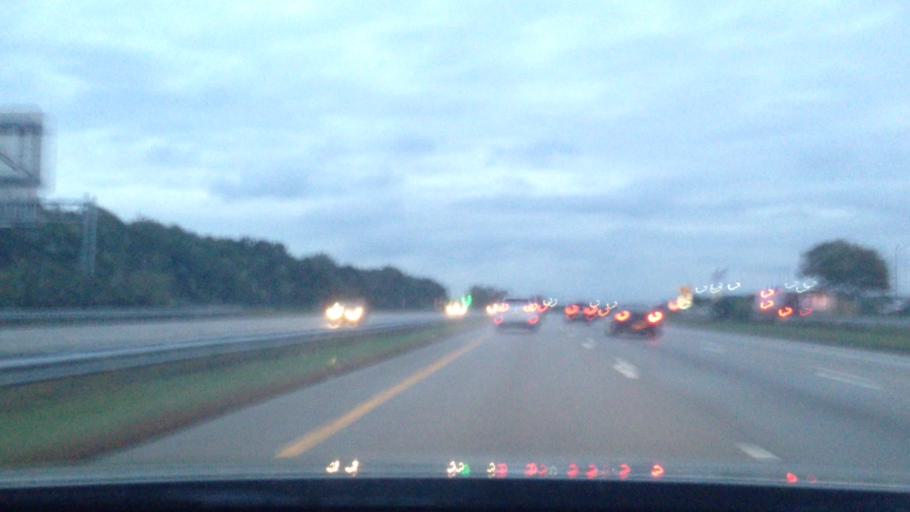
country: US
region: New York
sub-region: Suffolk County
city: Sayville
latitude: 40.7663
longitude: -73.0760
